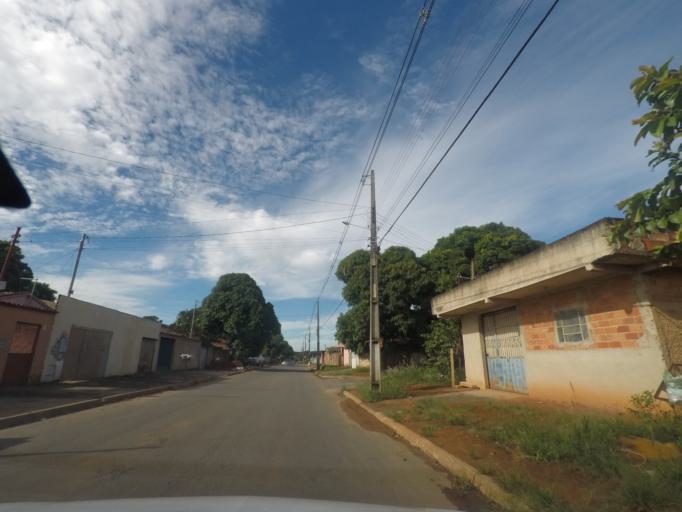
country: BR
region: Goias
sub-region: Aparecida De Goiania
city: Aparecida de Goiania
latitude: -16.8213
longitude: -49.2954
